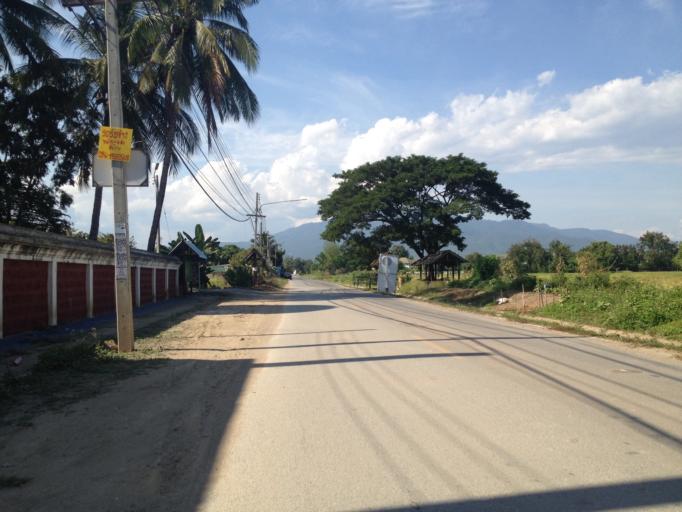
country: TH
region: Chiang Mai
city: Hang Dong
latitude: 18.7256
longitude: 98.9579
